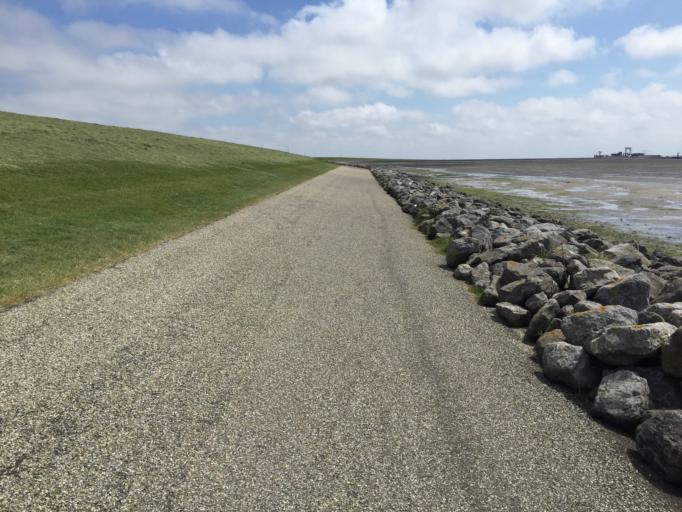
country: NL
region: Friesland
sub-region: Gemeente Schiermonnikoog
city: Schiermonnikoog
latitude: 53.4724
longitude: 6.1890
